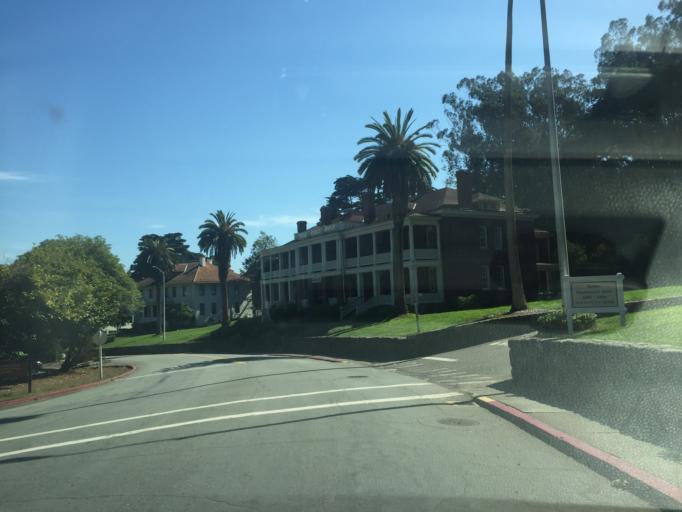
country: US
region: California
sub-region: San Francisco County
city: San Francisco
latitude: 37.7986
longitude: -122.4738
